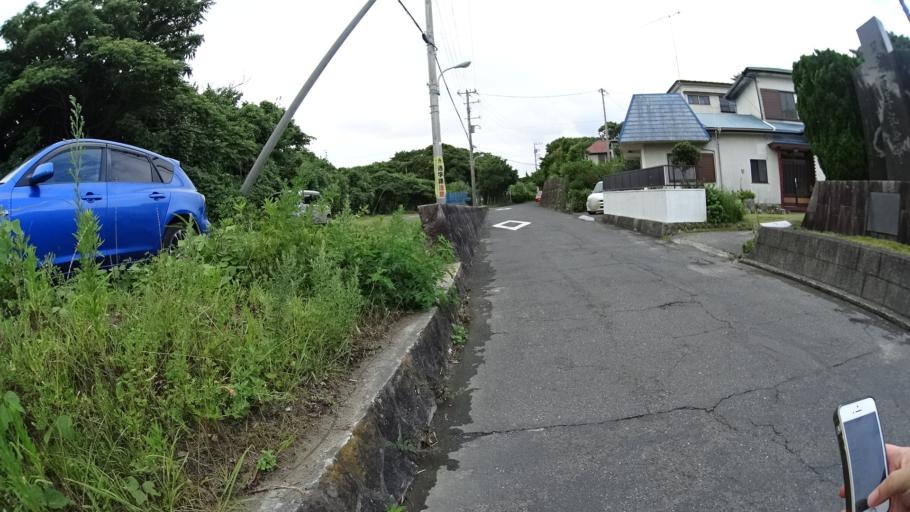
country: JP
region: Shizuoka
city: Shimoda
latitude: 34.3256
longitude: 139.2161
